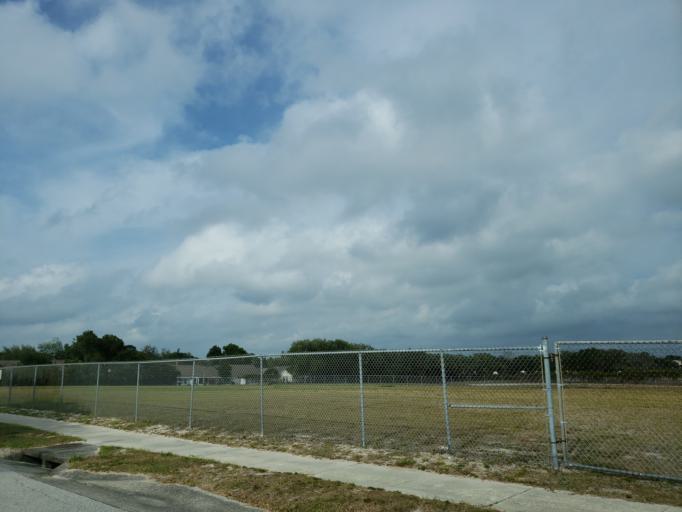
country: US
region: Florida
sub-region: Pinellas County
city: Saint George
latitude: 28.0883
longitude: -82.7297
